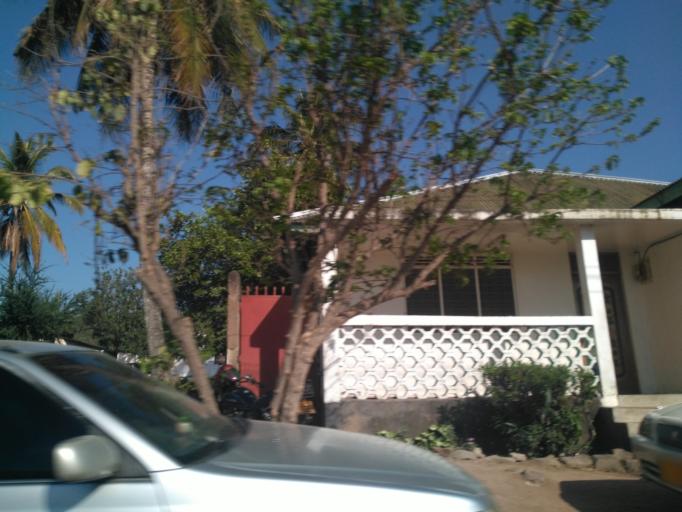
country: TZ
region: Mwanza
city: Mwanza
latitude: -2.5028
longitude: 32.8954
